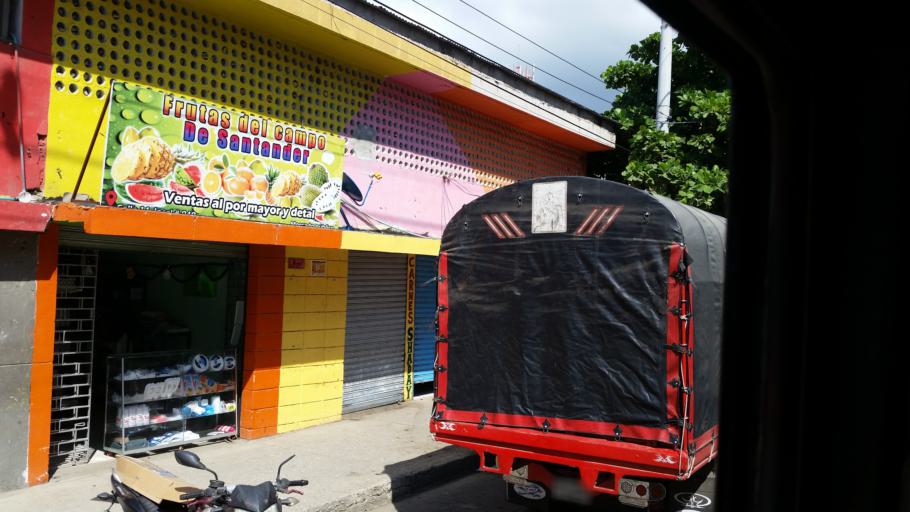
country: CO
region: Magdalena
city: Santa Marta
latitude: 11.2458
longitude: -74.2059
